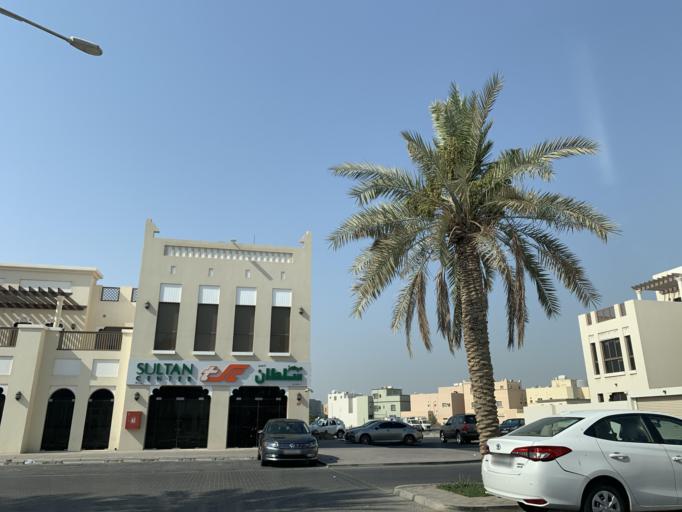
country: BH
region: Northern
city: Madinat `Isa
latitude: 26.1946
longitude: 50.5114
